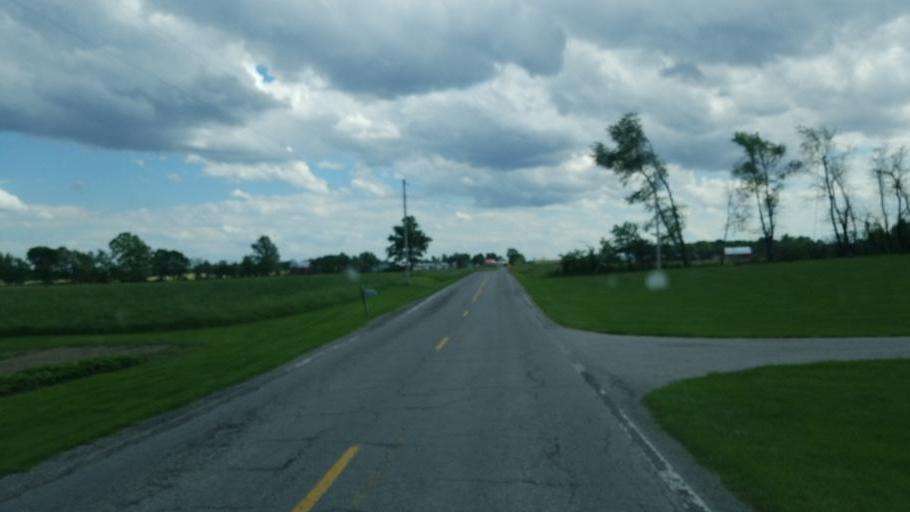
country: US
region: Ohio
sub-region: Huron County
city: Plymouth
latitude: 41.0003
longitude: -82.6064
